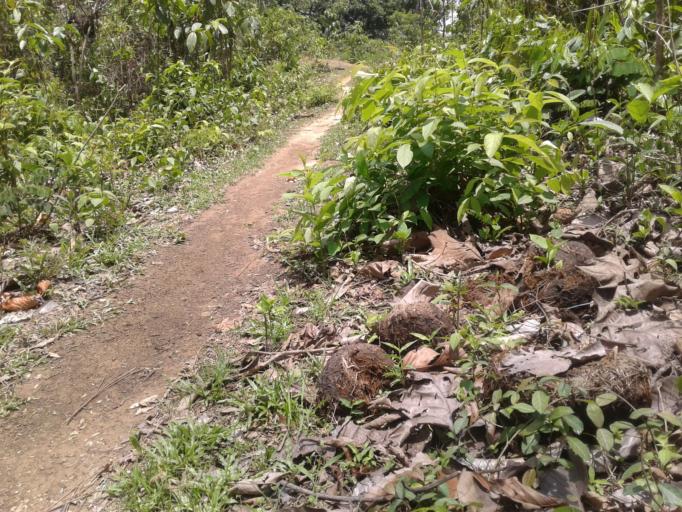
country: BD
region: Chittagong
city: Cox's Bazar
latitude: 21.6926
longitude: 92.0874
